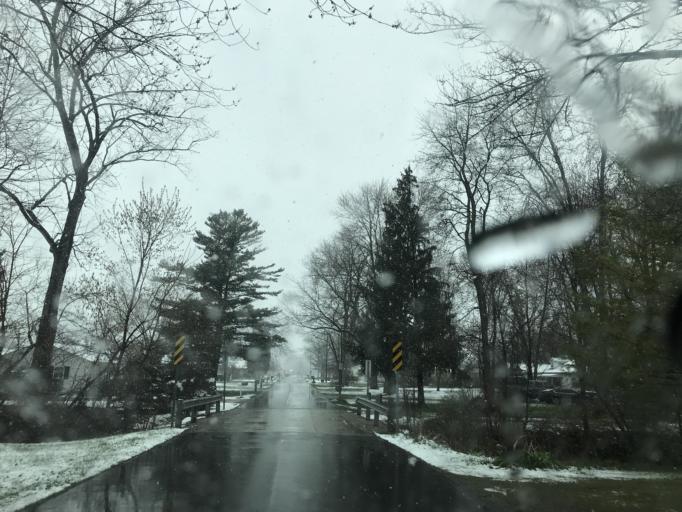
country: US
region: Michigan
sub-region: Wayne County
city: Taylor
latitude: 42.2286
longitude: -83.2480
